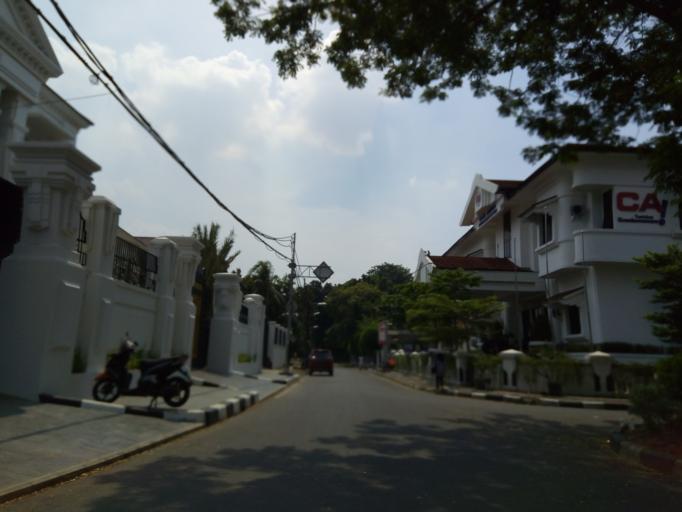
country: ID
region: Jakarta Raya
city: Jakarta
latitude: -6.2051
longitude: 106.8412
